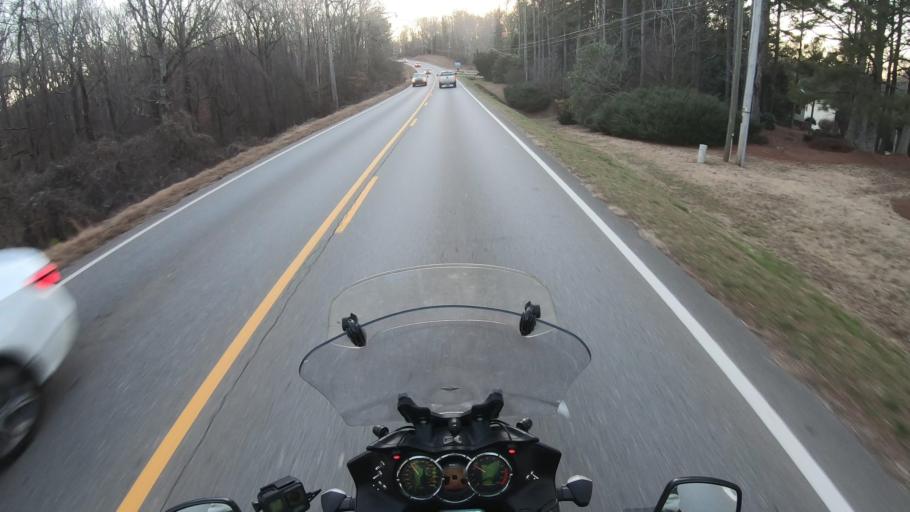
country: US
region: Georgia
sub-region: Cherokee County
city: Ball Ground
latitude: 34.2824
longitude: -84.2915
